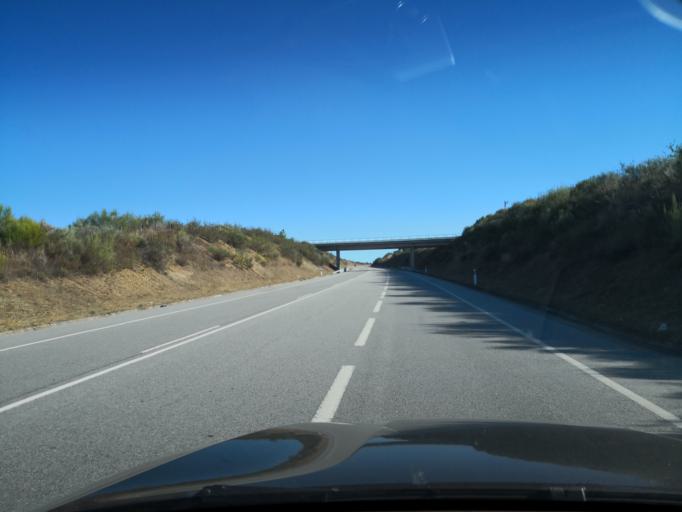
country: PT
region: Braganca
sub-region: Mirandela
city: Mirandela
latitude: 41.4927
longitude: -7.2266
